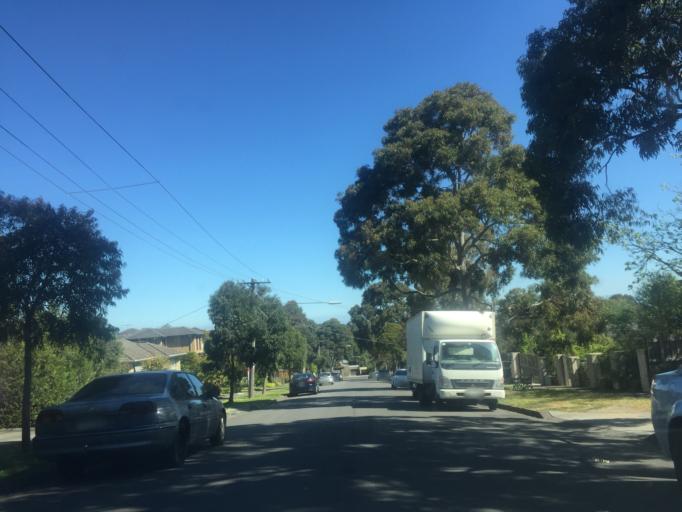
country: AU
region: Victoria
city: Mont Albert
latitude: -37.8122
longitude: 145.0910
